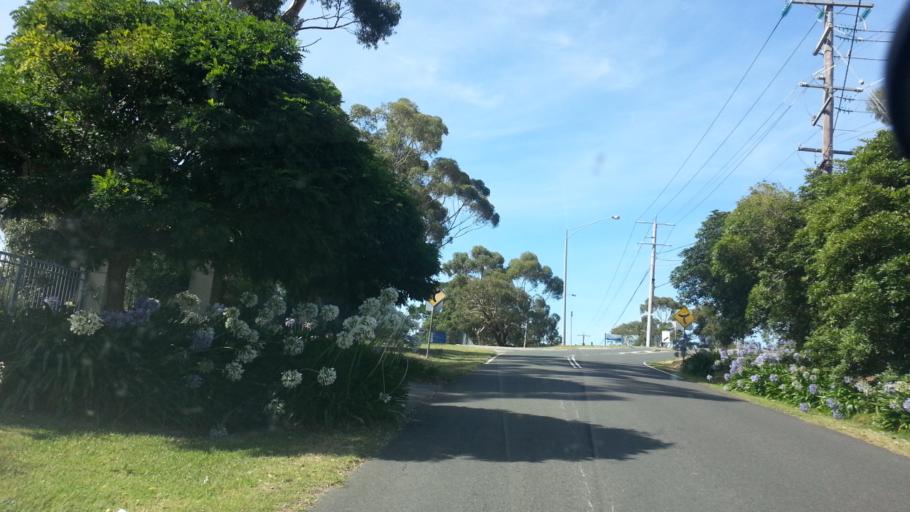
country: AU
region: Victoria
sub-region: Casey
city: Endeavour Hills
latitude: -37.9615
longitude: 145.2823
